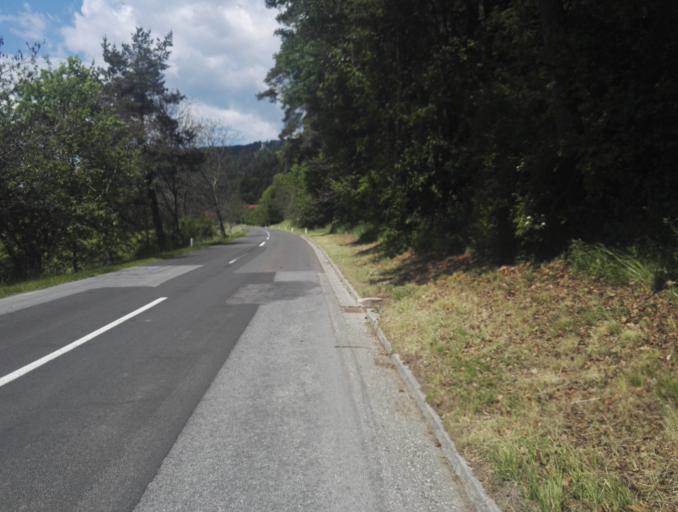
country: AT
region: Styria
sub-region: Politischer Bezirk Graz-Umgebung
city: Frohnleiten
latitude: 47.2219
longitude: 15.3020
